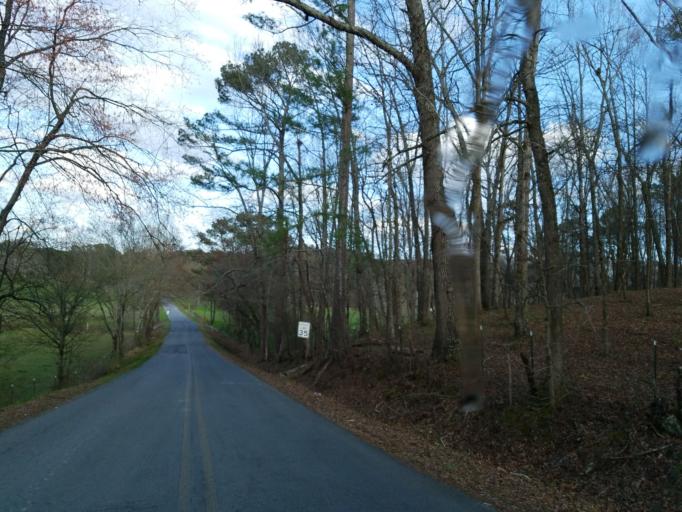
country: US
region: Georgia
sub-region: Bartow County
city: Rydal
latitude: 34.4787
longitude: -84.6763
